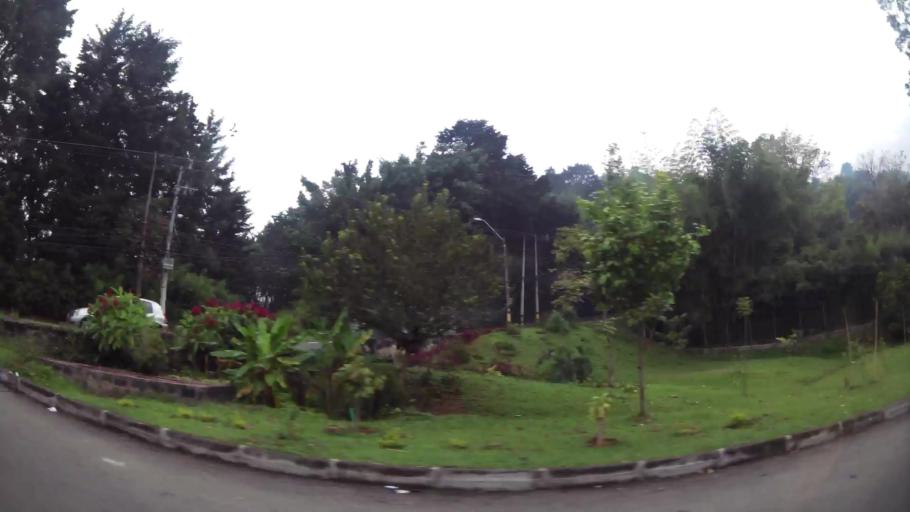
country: CO
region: Antioquia
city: Envigado
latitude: 6.1913
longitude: -75.5553
